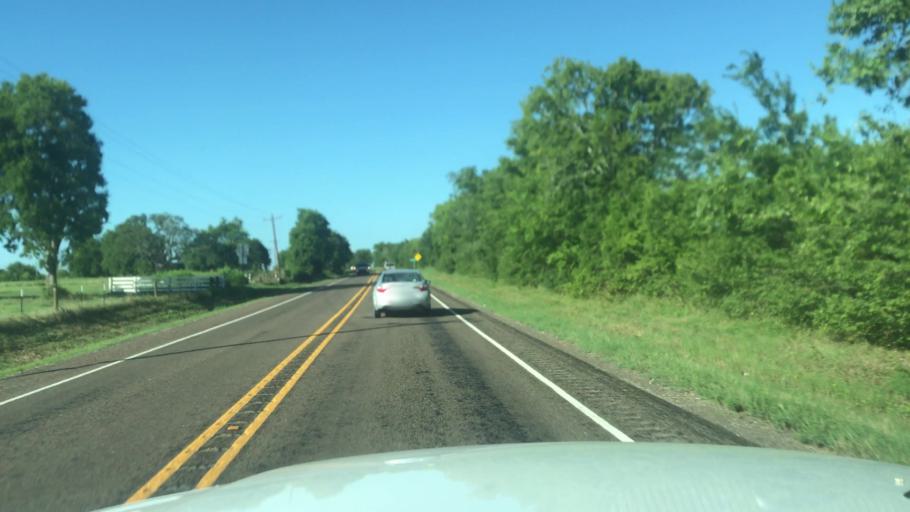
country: US
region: Texas
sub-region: Grimes County
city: Anderson
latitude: 30.6358
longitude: -95.8637
